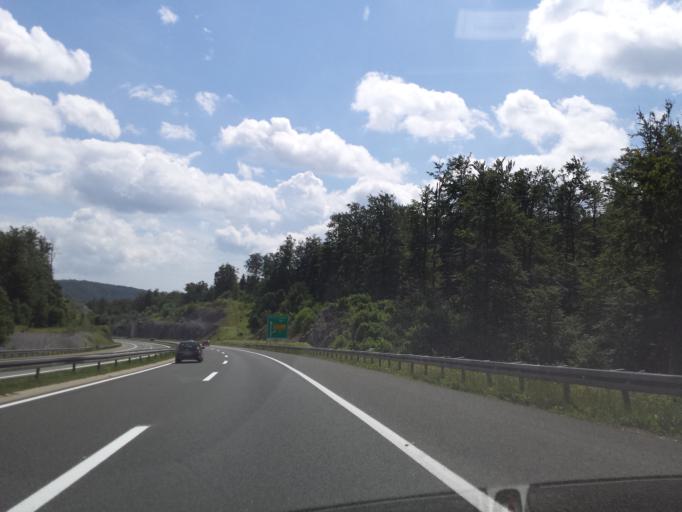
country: HR
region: Primorsko-Goranska
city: Vrbovsko
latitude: 45.3582
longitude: 15.0685
